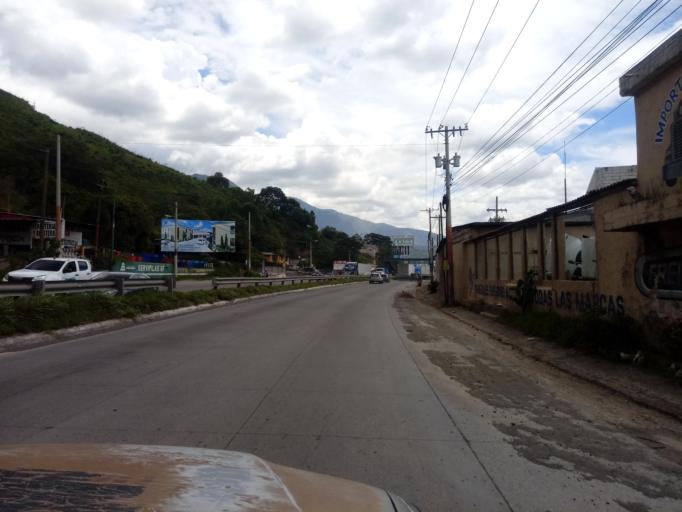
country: GT
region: Escuintla
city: San Vicente Pacaya
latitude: 14.4563
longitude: -90.6433
